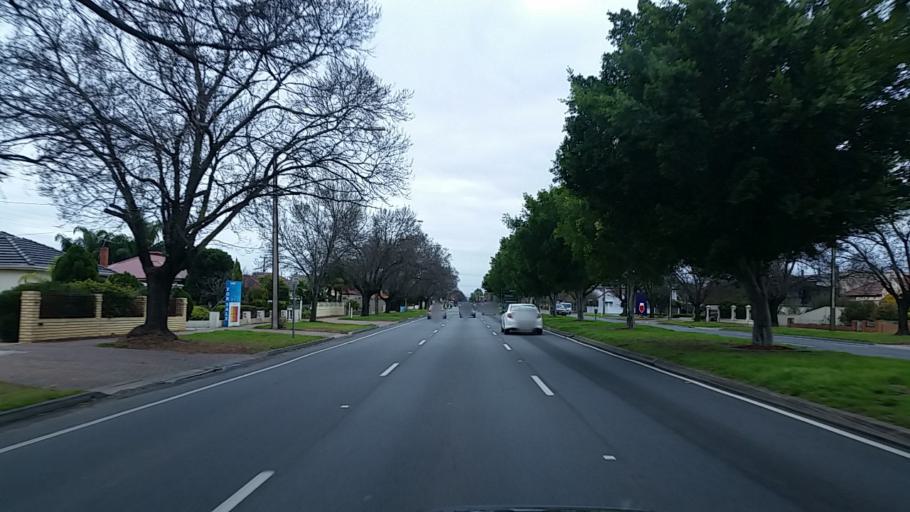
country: AU
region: South Australia
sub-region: Marion
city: Plympton Park
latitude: -34.9704
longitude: 138.5447
